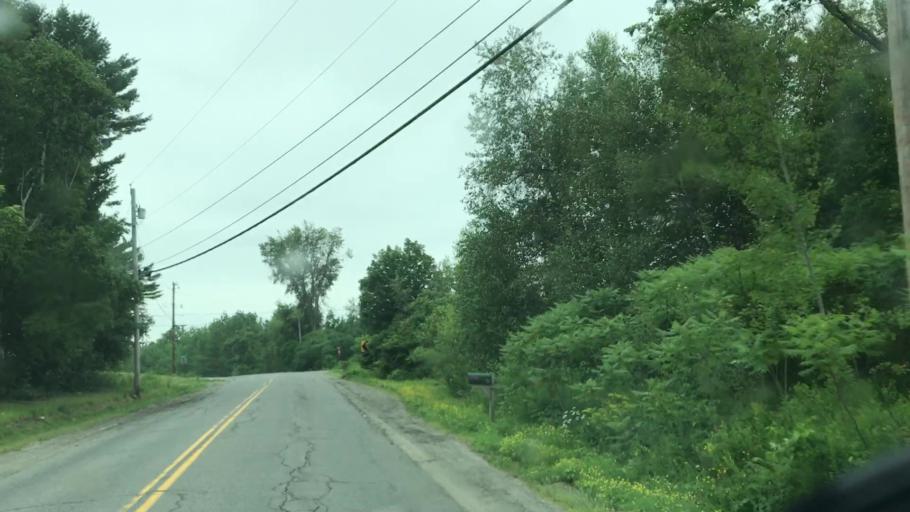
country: US
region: Maine
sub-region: Penobscot County
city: Orono
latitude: 44.8794
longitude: -68.7115
